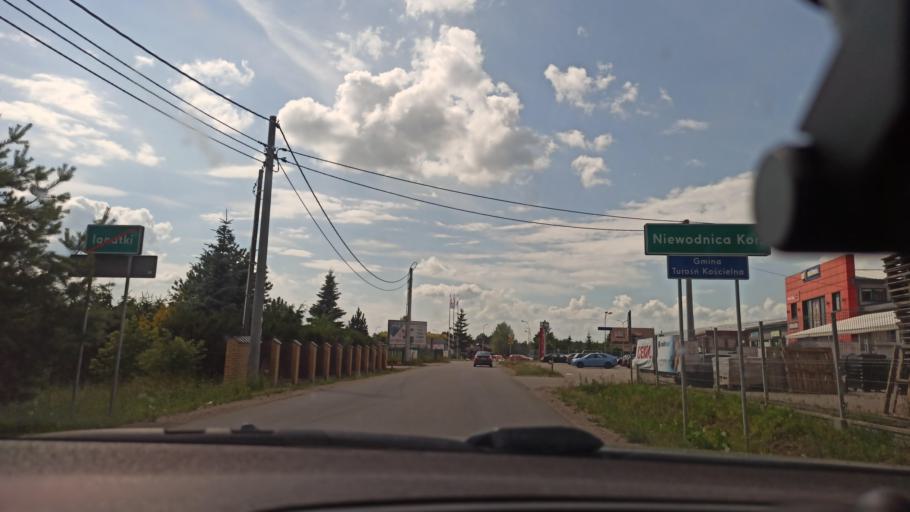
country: PL
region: Podlasie
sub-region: Powiat bialostocki
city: Turosn Koscielna
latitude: 53.0690
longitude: 23.0823
